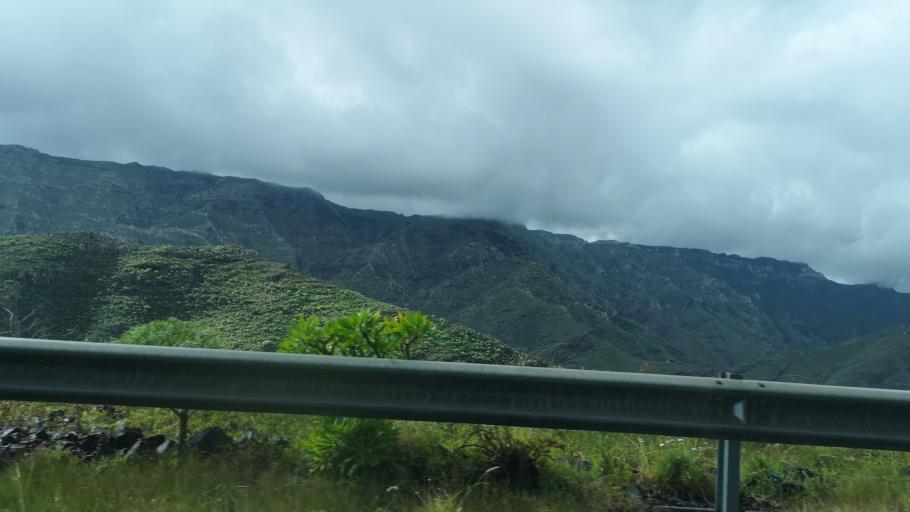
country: ES
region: Canary Islands
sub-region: Provincia de Santa Cruz de Tenerife
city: San Sebastian de la Gomera
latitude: 28.1219
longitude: -17.1523
